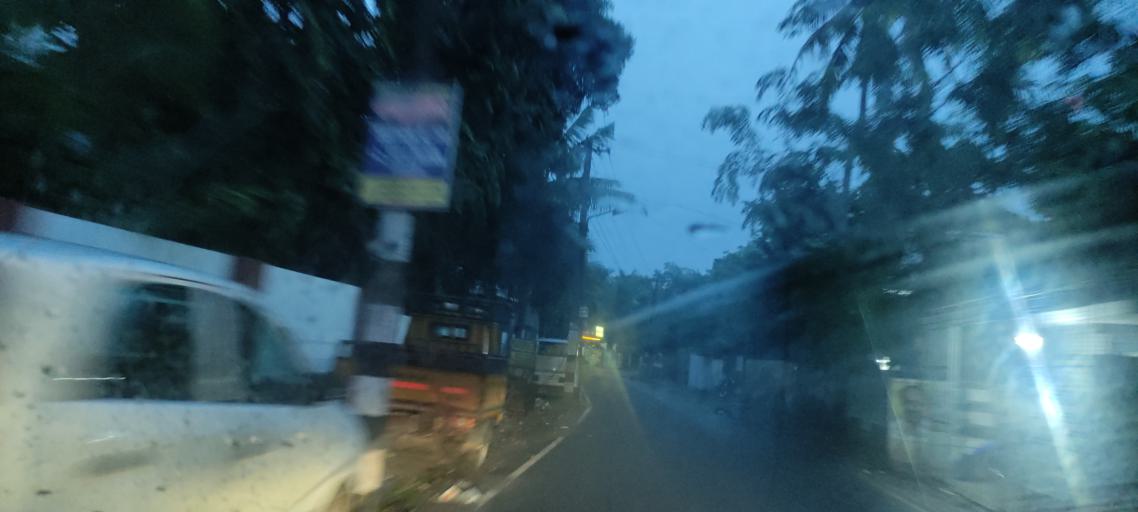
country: IN
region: Kerala
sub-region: Ernakulam
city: Cochin
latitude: 9.9141
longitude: 76.2918
